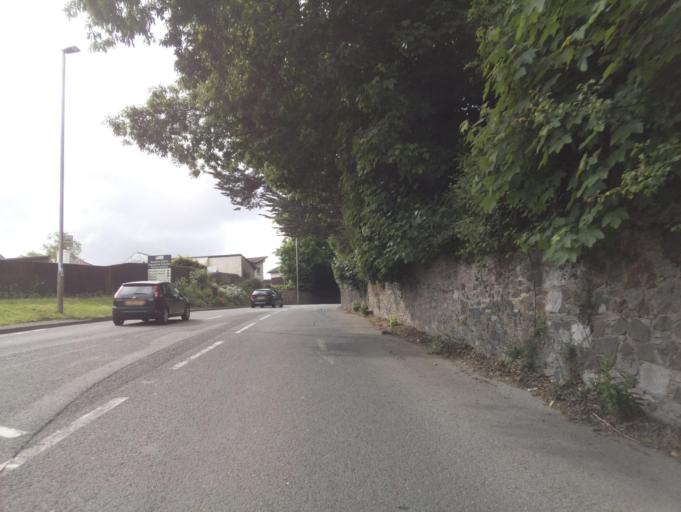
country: GB
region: England
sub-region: Devon
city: Newton Abbot
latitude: 50.5391
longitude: -3.6164
